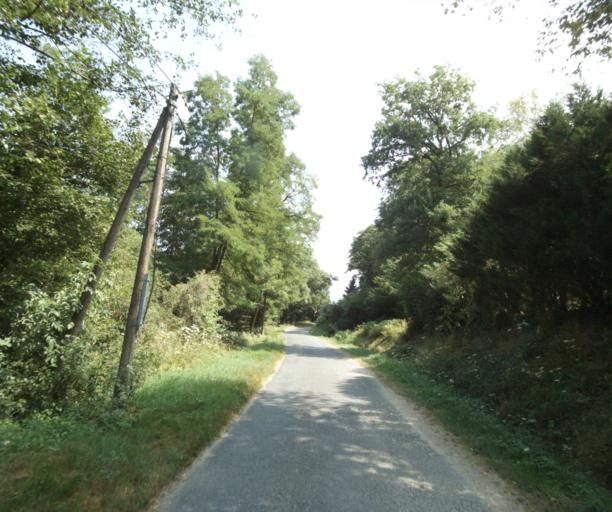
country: FR
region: Bourgogne
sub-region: Departement de Saone-et-Loire
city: Gueugnon
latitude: 46.6164
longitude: 4.0298
